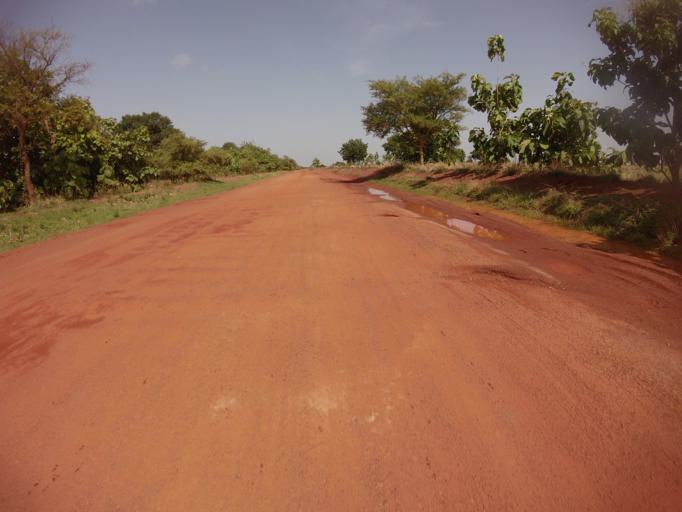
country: GH
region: Upper East
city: Bawku
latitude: 11.0050
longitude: -0.1994
